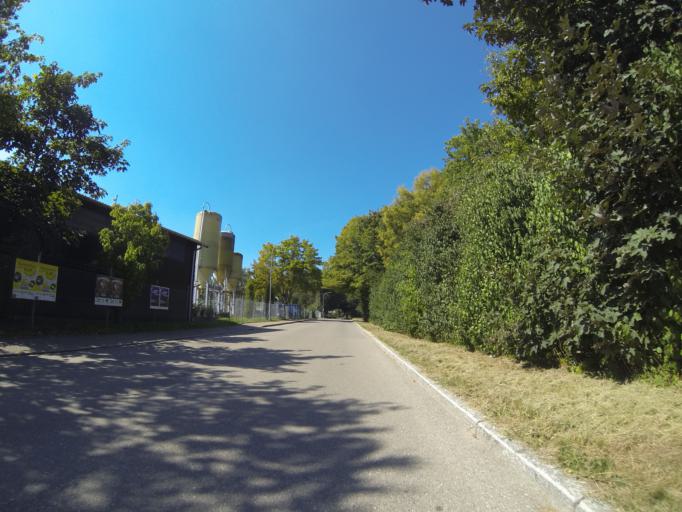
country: DE
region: Baden-Wuerttemberg
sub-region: Tuebingen Region
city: Erbach
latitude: 48.3268
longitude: 9.9055
